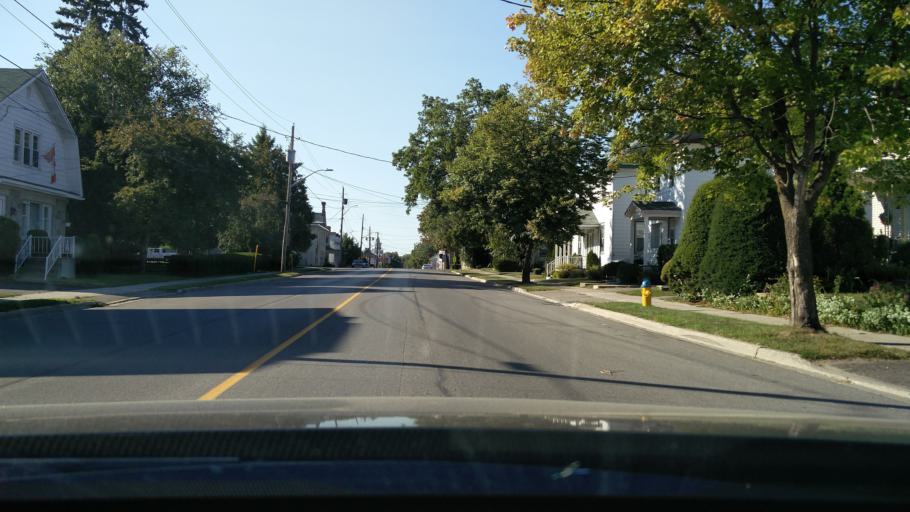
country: CA
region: Ontario
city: Perth
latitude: 44.8955
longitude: -76.2442
